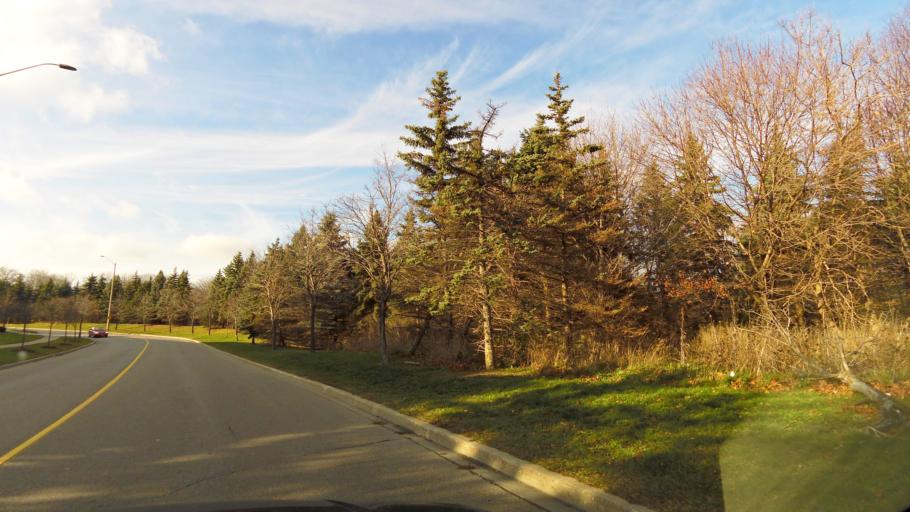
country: CA
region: Ontario
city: Mississauga
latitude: 43.5323
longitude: -79.6520
